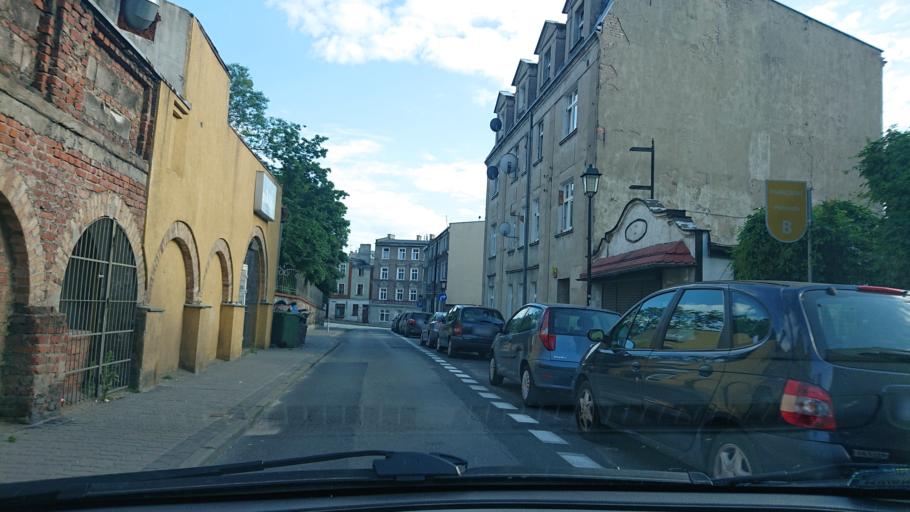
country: PL
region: Greater Poland Voivodeship
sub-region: Powiat gnieznienski
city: Gniezno
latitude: 52.5356
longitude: 17.5944
